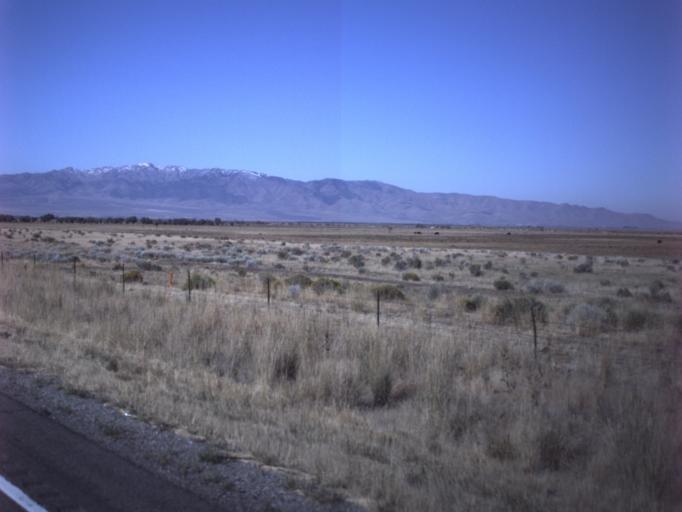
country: US
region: Utah
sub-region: Tooele County
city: Erda
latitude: 40.6338
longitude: -112.3332
